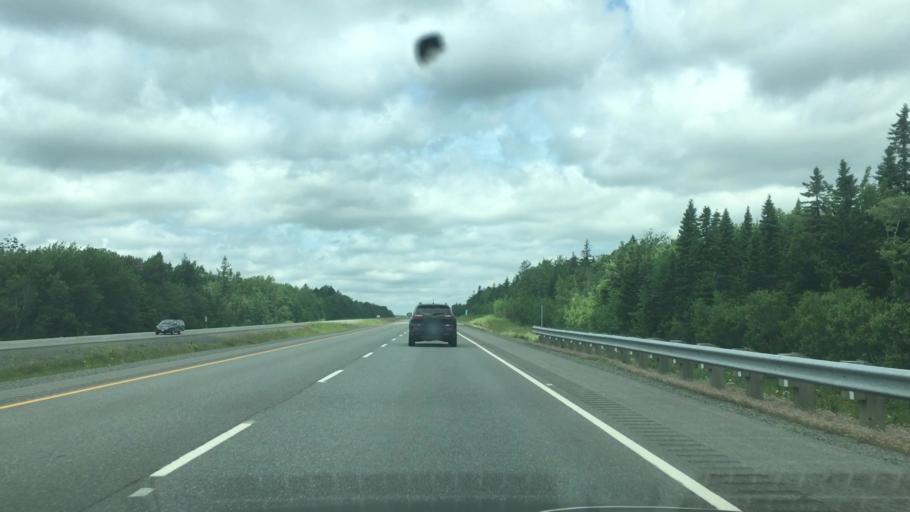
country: CA
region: Nova Scotia
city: Springhill
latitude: 45.7146
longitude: -64.0438
